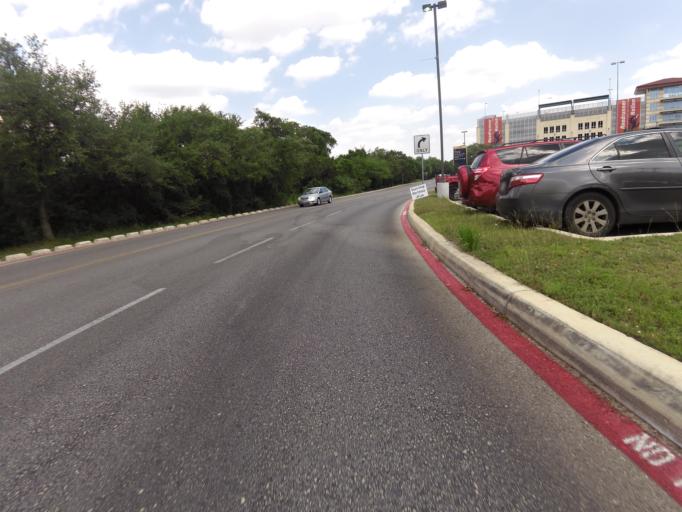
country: US
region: Texas
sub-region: Bexar County
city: Shavano Park
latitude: 29.5874
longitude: -98.6180
